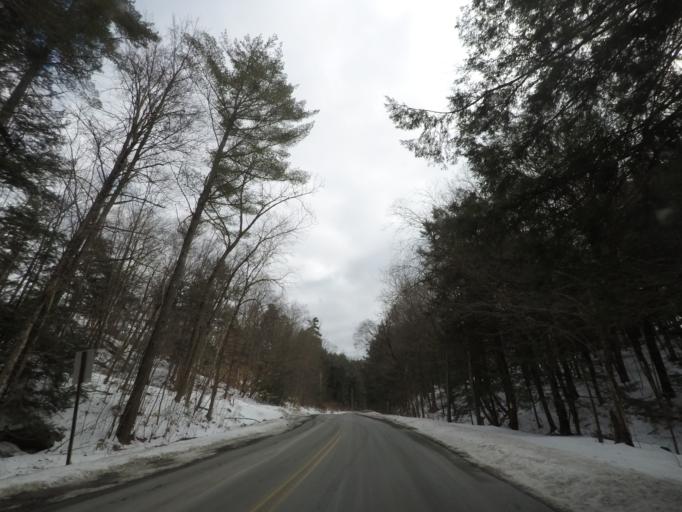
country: US
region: New York
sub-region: Rensselaer County
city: Hoosick Falls
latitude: 42.8810
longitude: -73.4149
